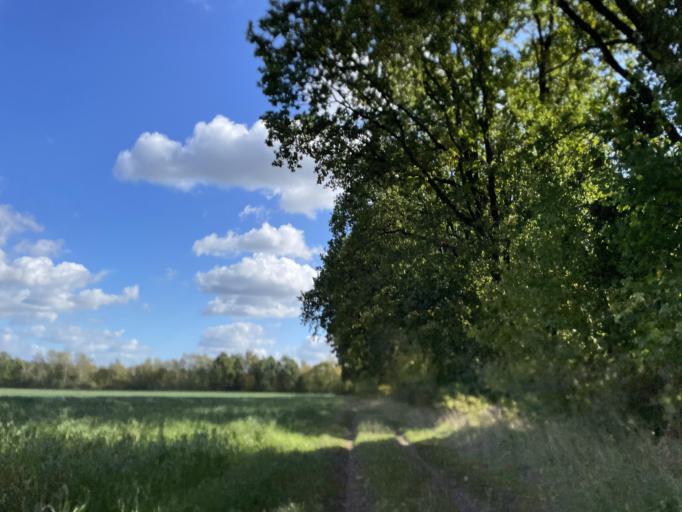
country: DE
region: Lower Saxony
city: Wendisch Evern
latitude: 53.2186
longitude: 10.4885
